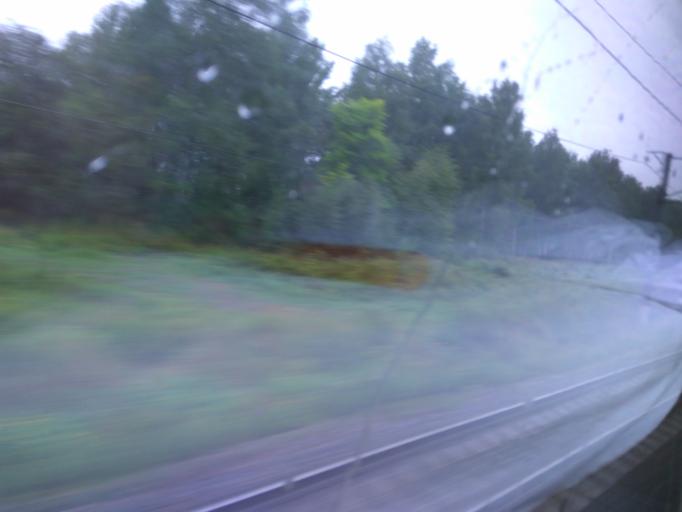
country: RU
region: Moskovskaya
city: Ozherel'ye
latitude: 54.8408
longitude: 38.2323
